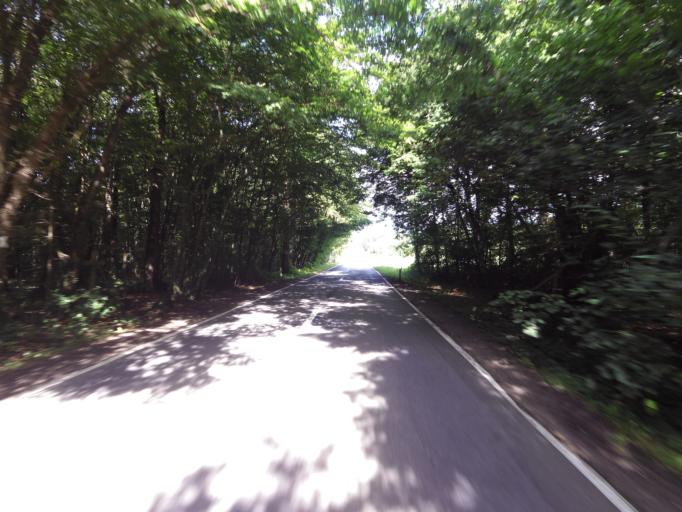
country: BE
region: Wallonia
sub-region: Province du Luxembourg
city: Hotton
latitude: 50.2784
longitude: 5.4857
